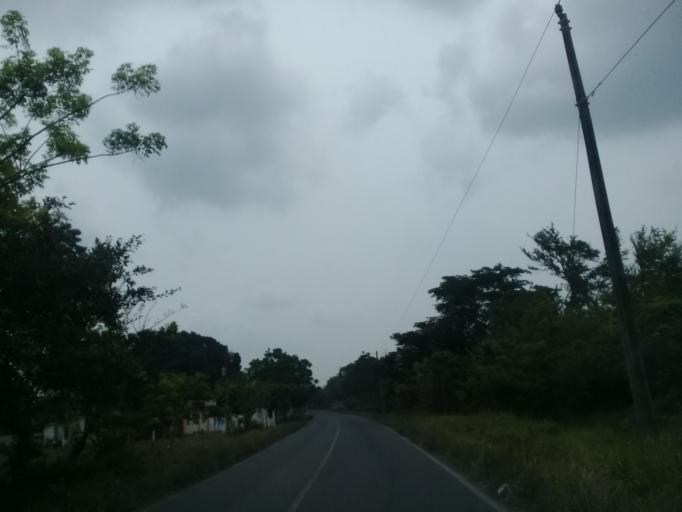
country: MX
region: Veracruz
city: Jamapa
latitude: 19.0540
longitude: -96.1999
